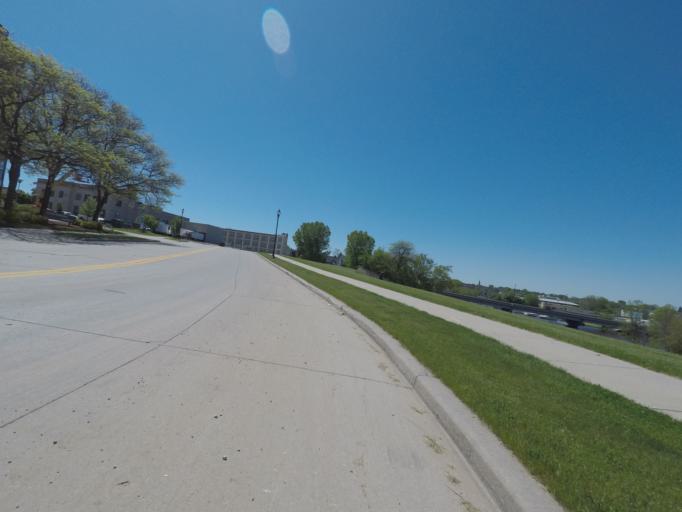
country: US
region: Wisconsin
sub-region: Sheboygan County
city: Sheboygan
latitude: 43.7515
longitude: -87.7163
